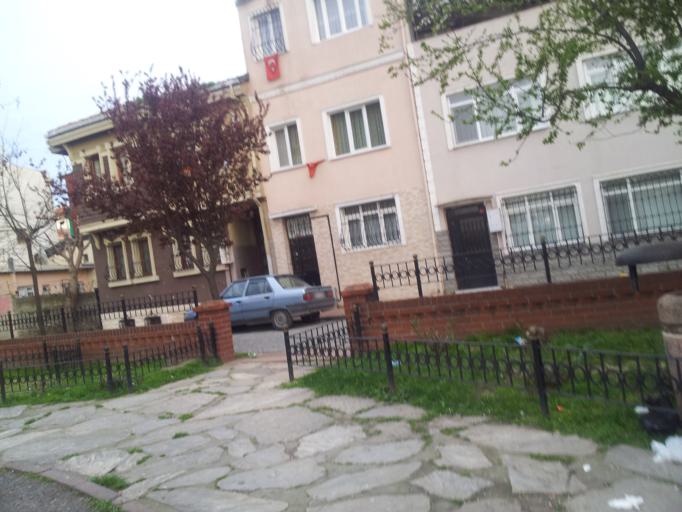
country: TR
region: Istanbul
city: Istanbul
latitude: 41.0337
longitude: 28.9401
